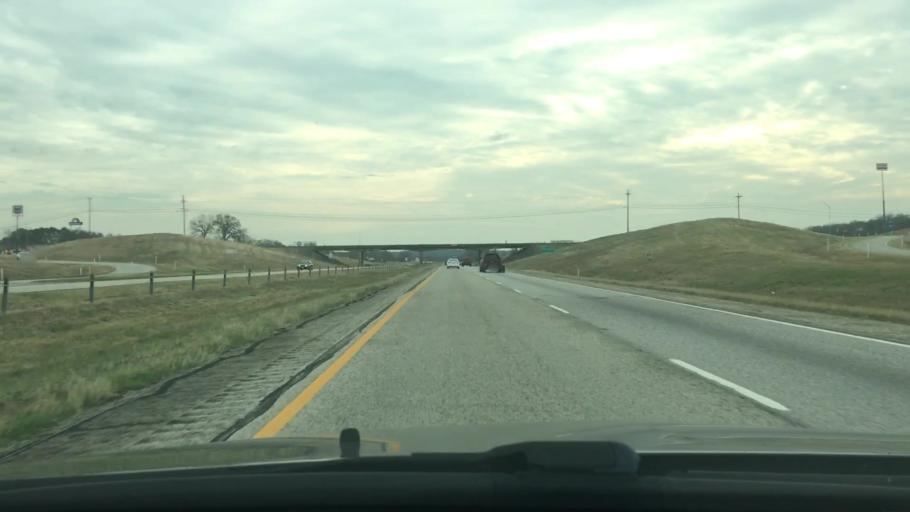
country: US
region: Texas
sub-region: Leon County
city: Centerville
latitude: 31.2607
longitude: -95.9879
